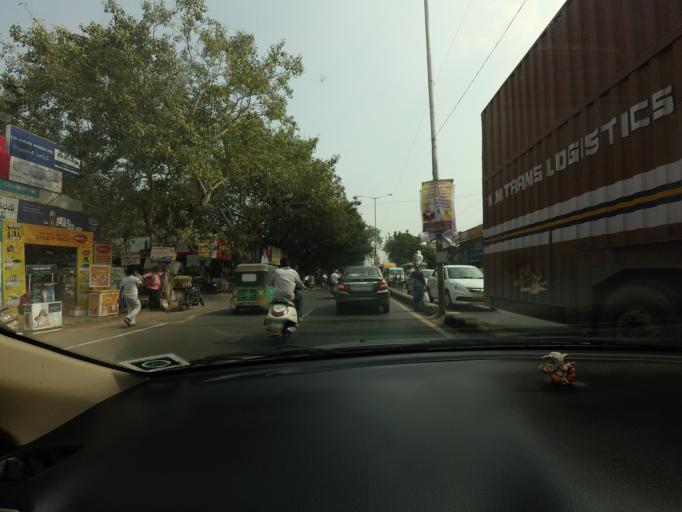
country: IN
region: Andhra Pradesh
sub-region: Krishna
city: Yanamalakuduru
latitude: 16.4944
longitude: 80.6625
